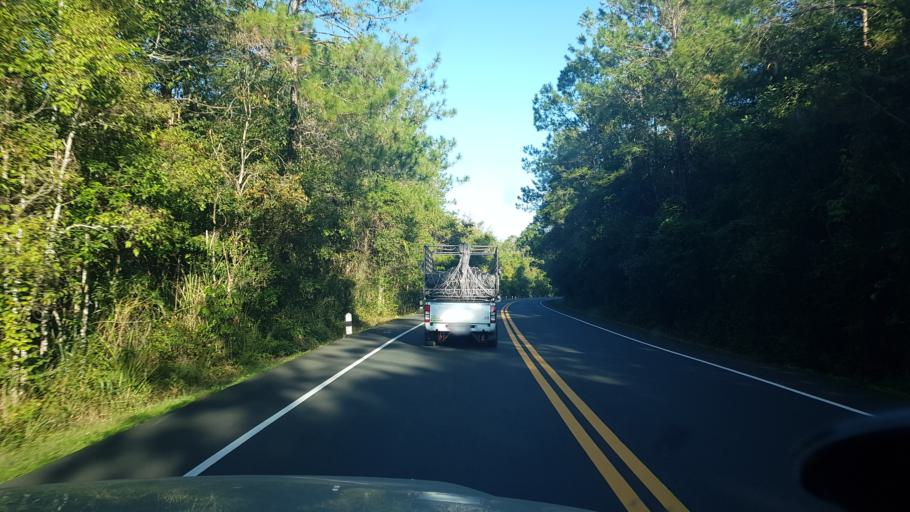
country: TH
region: Phetchabun
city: Nam Nao
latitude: 16.7109
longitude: 101.5982
